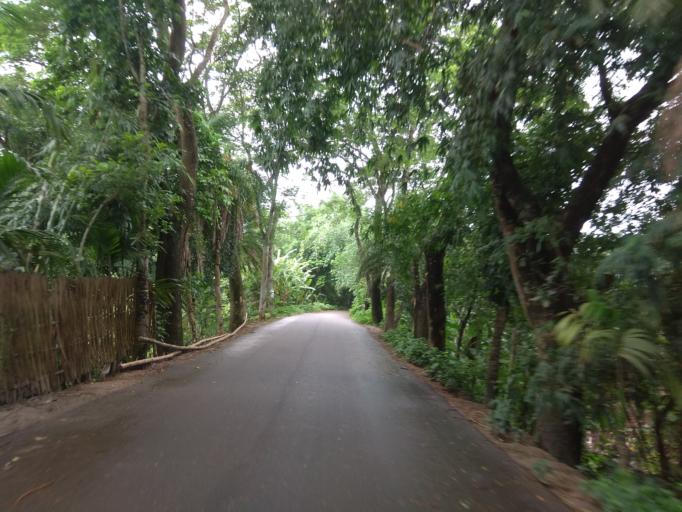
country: BD
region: Dhaka
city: Dohar
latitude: 23.4276
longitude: 90.0672
